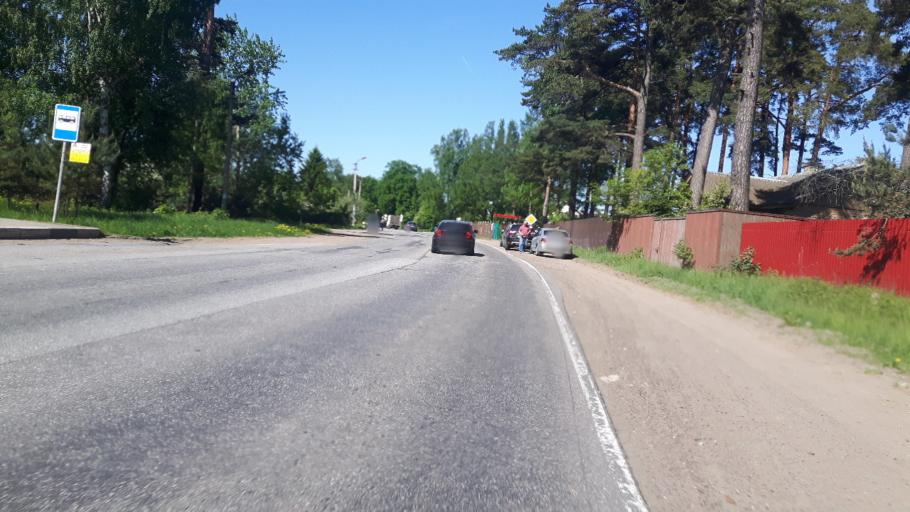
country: RU
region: Leningrad
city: Lebyazh'ye
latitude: 59.9606
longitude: 29.4319
